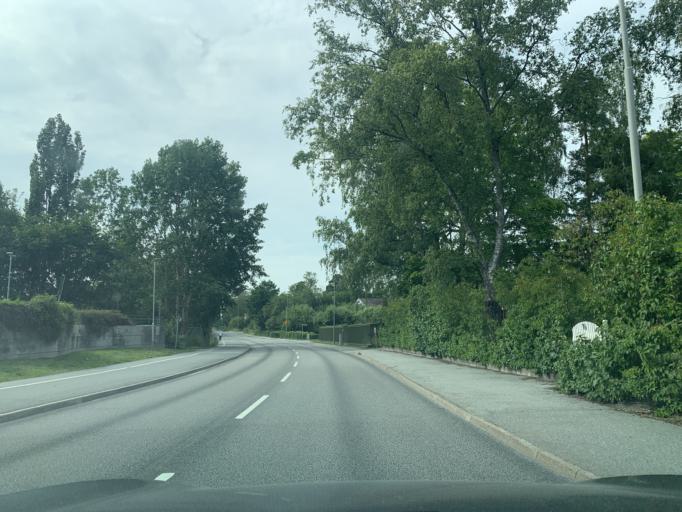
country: SE
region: Stockholm
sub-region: Norrtalje Kommun
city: Bergshamra
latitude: 59.3996
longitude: 18.0313
